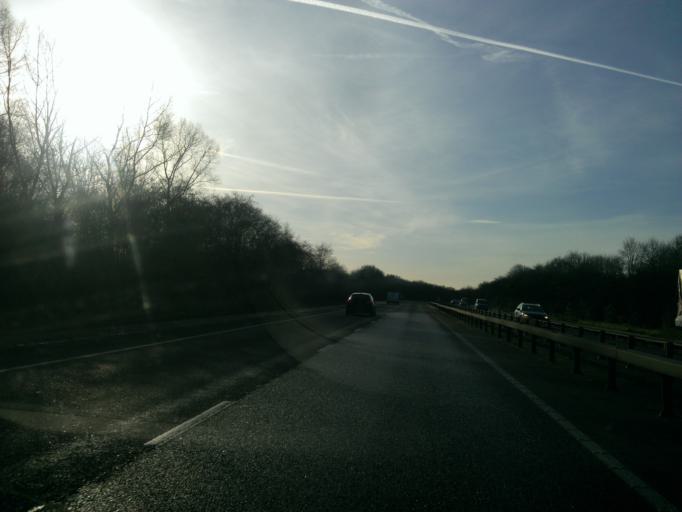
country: GB
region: England
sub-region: Essex
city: Witham
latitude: 51.7973
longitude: 0.6518
